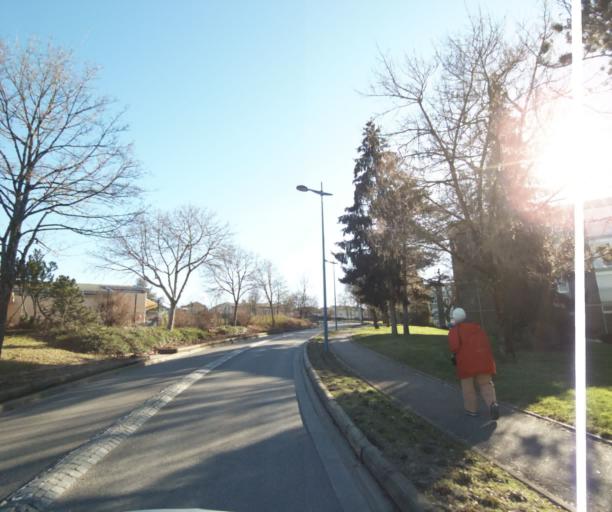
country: FR
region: Lorraine
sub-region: Departement de Meurthe-et-Moselle
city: Vandoeuvre-les-Nancy
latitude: 48.6464
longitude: 6.1974
